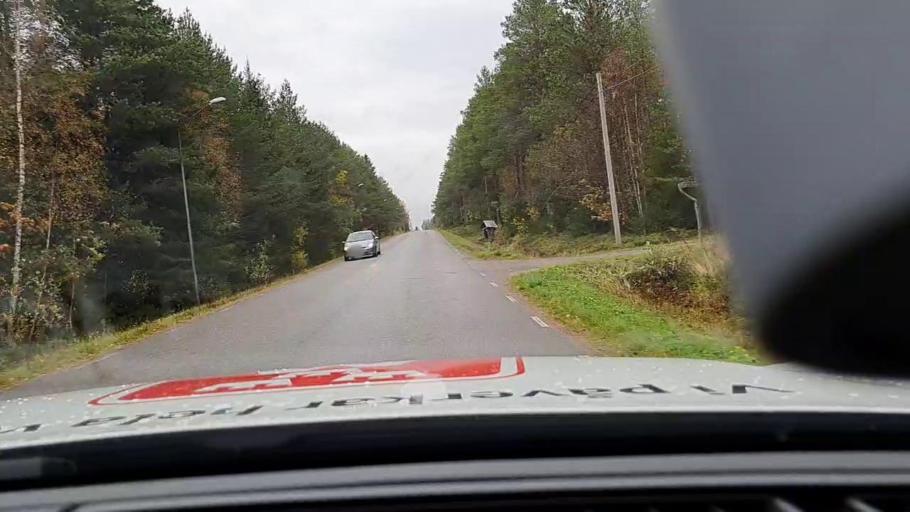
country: SE
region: Norrbotten
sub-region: Haparanda Kommun
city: Haparanda
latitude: 65.7873
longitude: 23.9211
